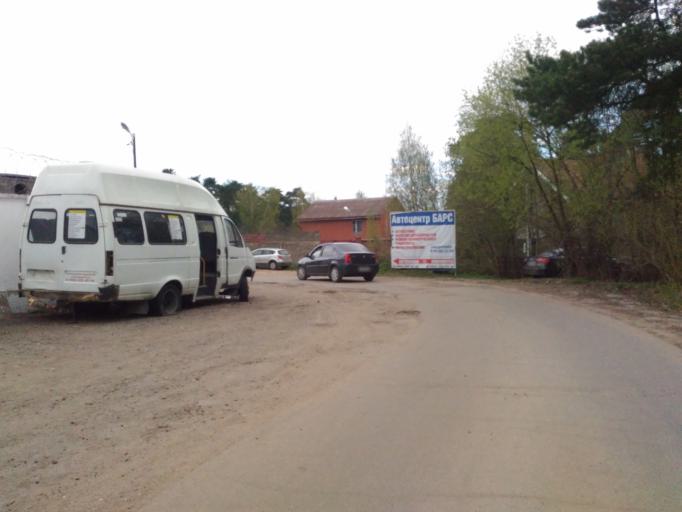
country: RU
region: Moskovskaya
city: Nakhabino
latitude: 55.8470
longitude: 37.1639
